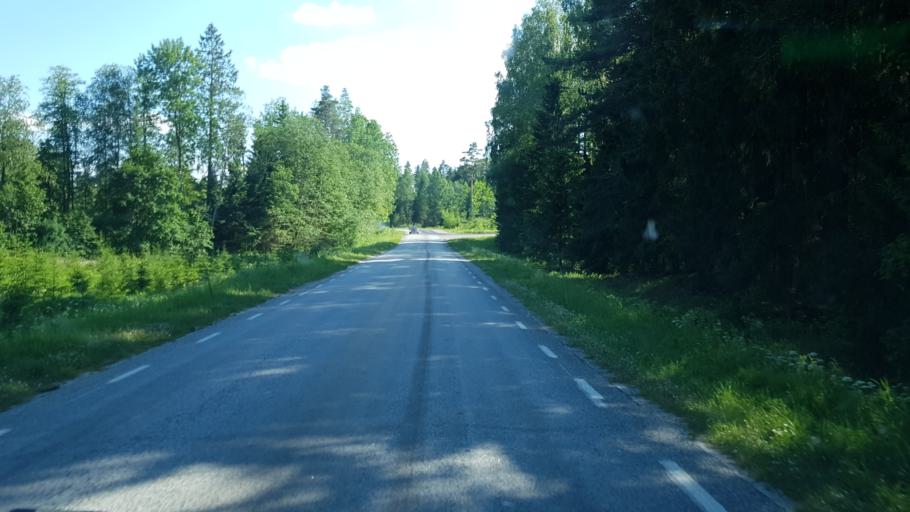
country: EE
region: Vorumaa
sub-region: Voru linn
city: Voru
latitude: 57.7498
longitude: 26.9170
